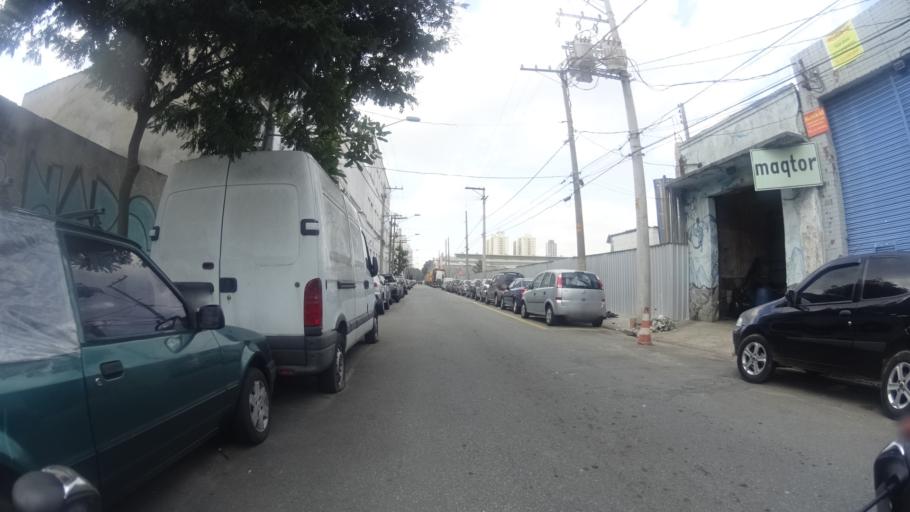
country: BR
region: Sao Paulo
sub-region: Sao Paulo
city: Sao Paulo
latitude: -23.5511
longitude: -46.6164
